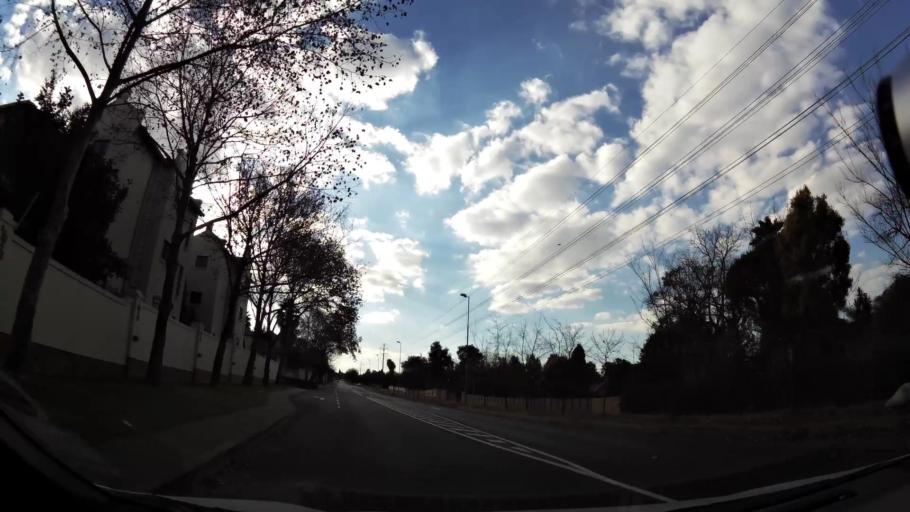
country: ZA
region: Gauteng
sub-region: City of Johannesburg Metropolitan Municipality
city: Diepsloot
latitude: -26.0186
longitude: 28.0209
